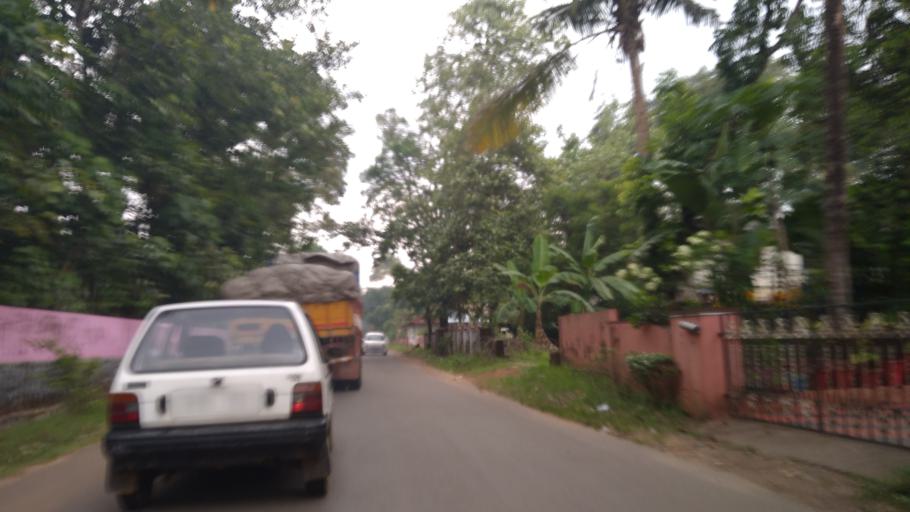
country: IN
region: Kerala
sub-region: Ernakulam
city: Perumbavoor
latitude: 10.0865
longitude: 76.5046
